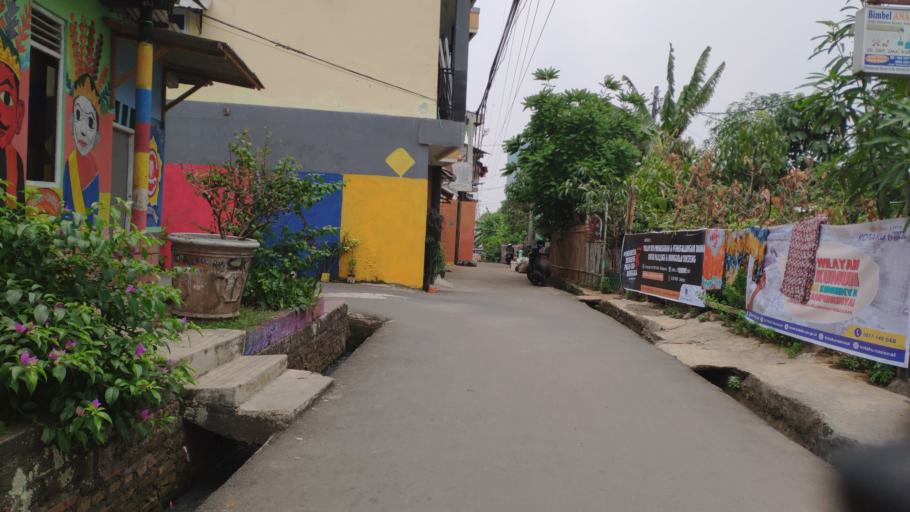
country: ID
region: West Java
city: Depok
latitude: -6.3076
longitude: 106.8321
